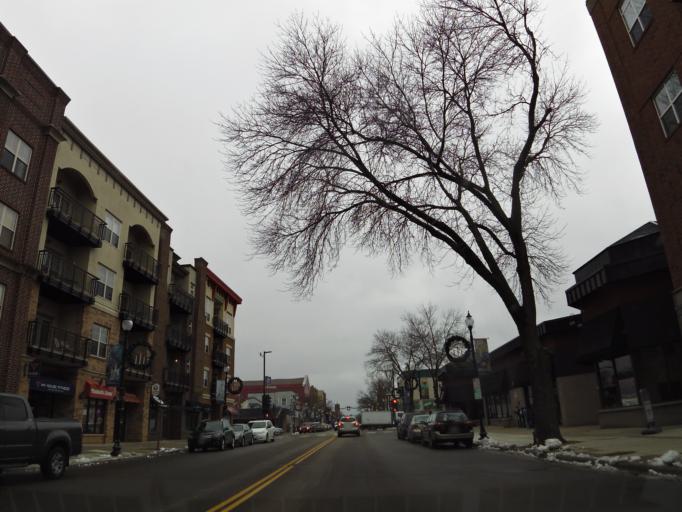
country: US
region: Minnesota
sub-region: Hennepin County
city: Minnetonka Mills
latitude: 44.9244
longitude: -93.4092
